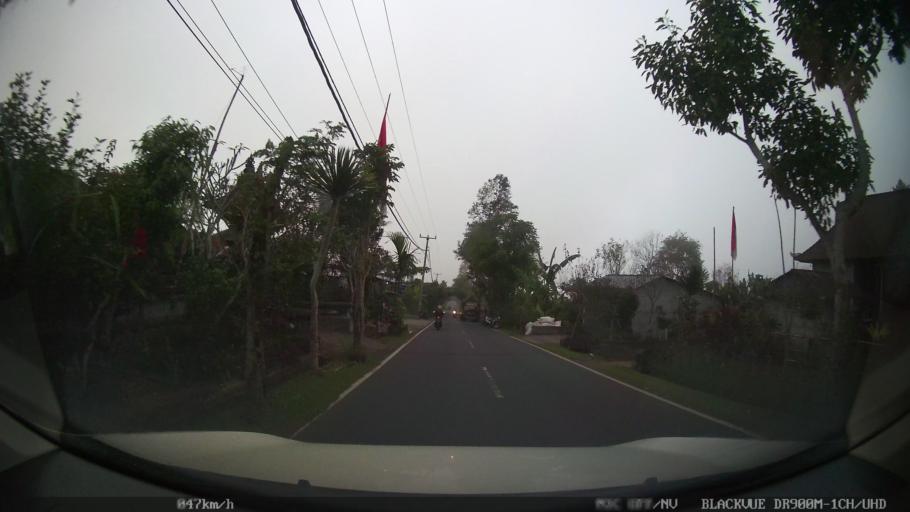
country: ID
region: Bali
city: Banjar Kedisan
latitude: -8.2941
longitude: 115.3150
